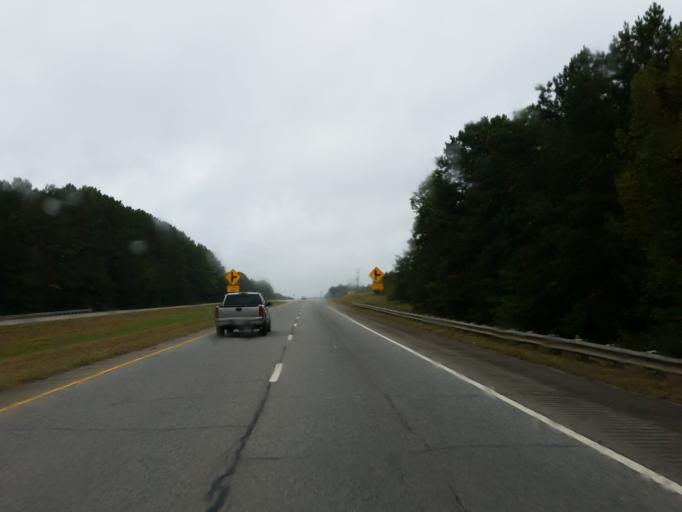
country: US
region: Georgia
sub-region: Lamar County
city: Barnesville
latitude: 33.0964
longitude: -84.1790
